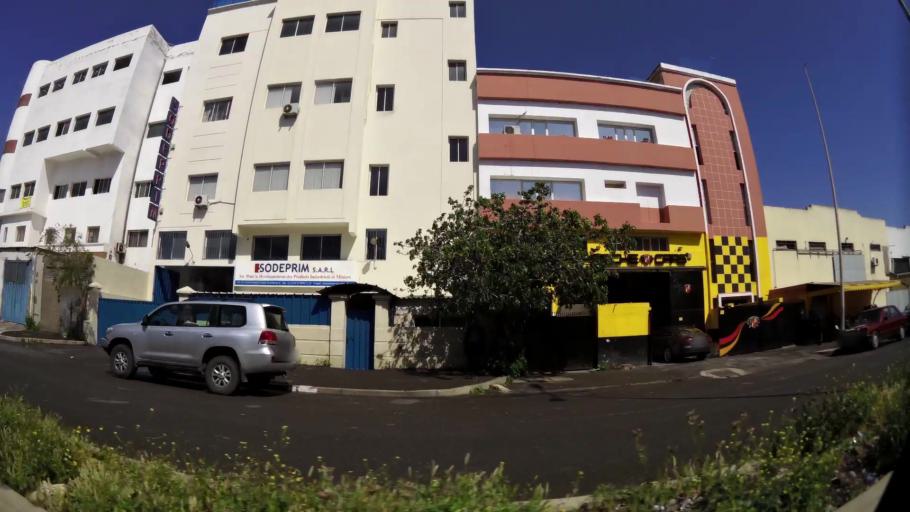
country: MA
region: Grand Casablanca
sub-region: Mediouna
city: Tit Mellil
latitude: 33.6179
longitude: -7.5065
